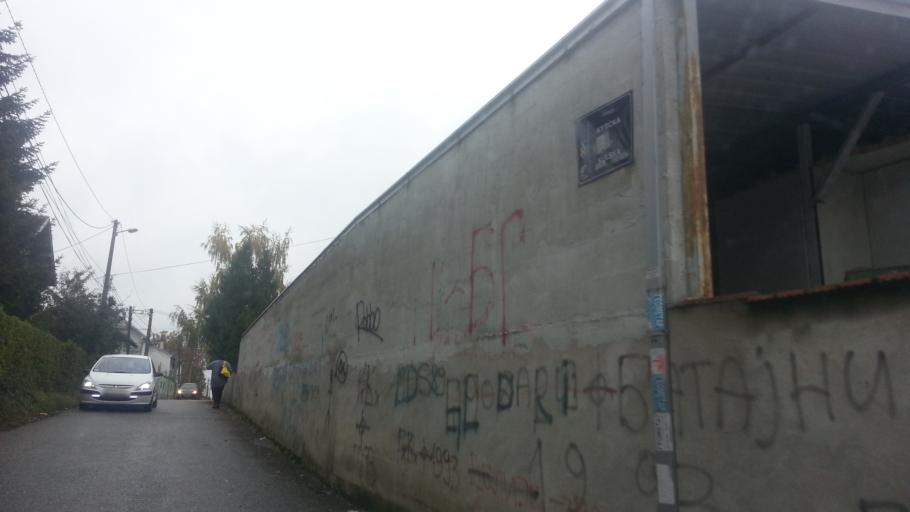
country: RS
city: Novi Banovci
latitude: 44.9011
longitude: 20.2951
